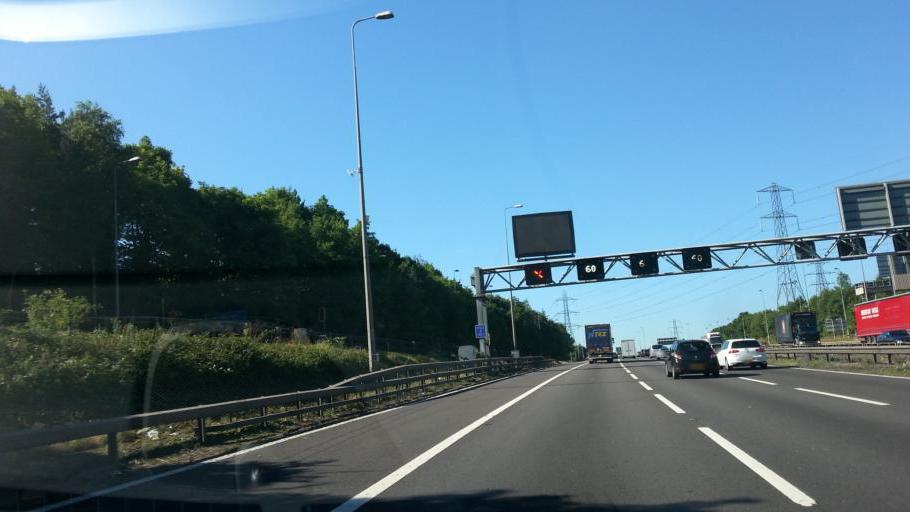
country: GB
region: England
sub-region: Solihull
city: Bickenhill
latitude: 52.4433
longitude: -1.7106
